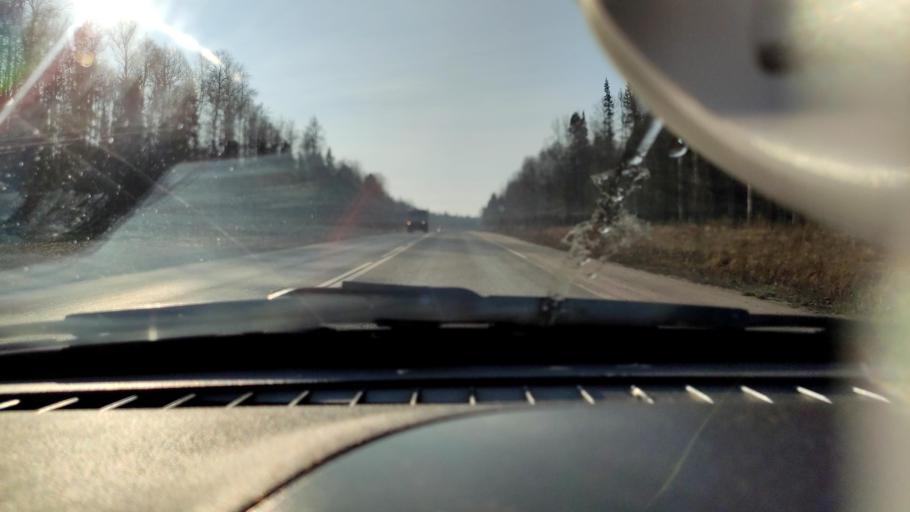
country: RU
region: Perm
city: Novyye Lyady
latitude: 58.0421
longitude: 56.5414
